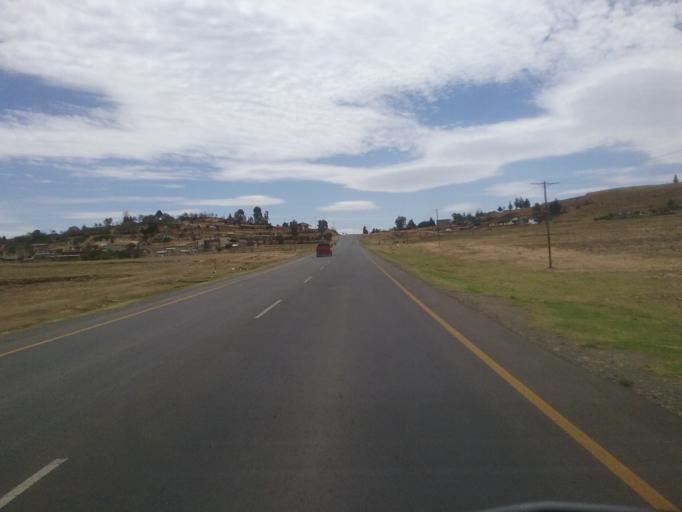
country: LS
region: Maseru
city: Maseru
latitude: -29.4969
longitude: 27.5283
